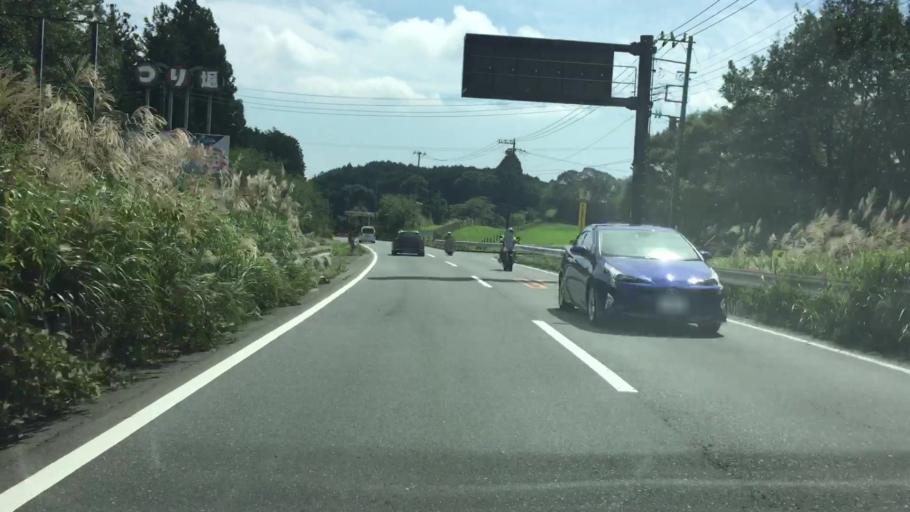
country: JP
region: Shizuoka
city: Fujinomiya
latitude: 35.3547
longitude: 138.5797
